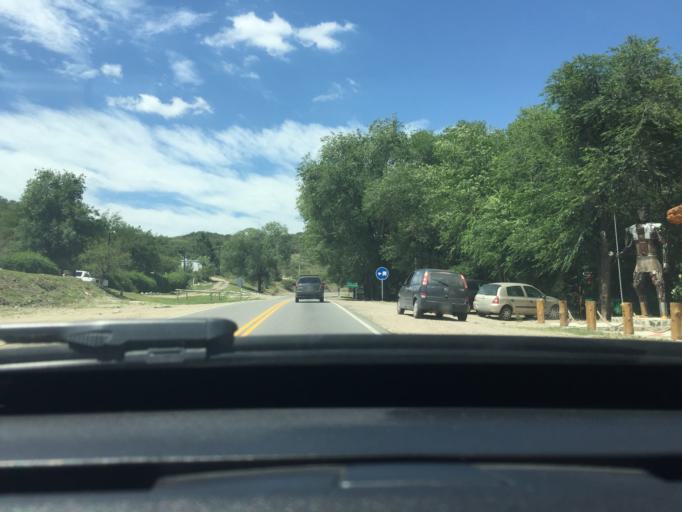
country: AR
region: Cordoba
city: Alta Gracia
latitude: -31.7379
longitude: -64.4527
